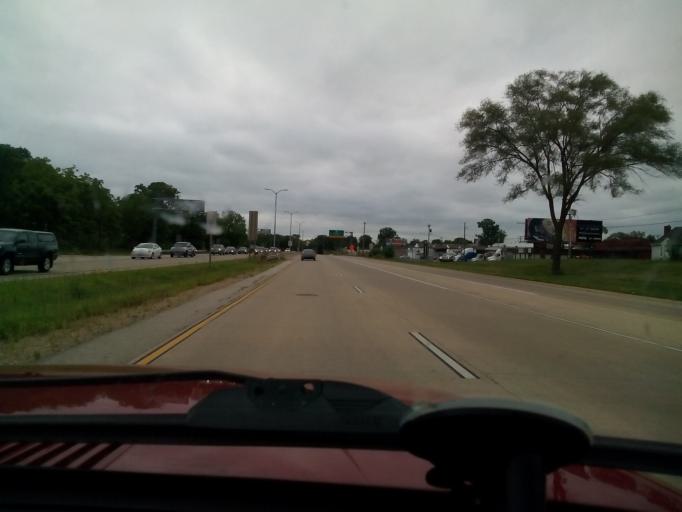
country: US
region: Wisconsin
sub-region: Dane County
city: Monona
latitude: 43.1067
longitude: -89.3330
